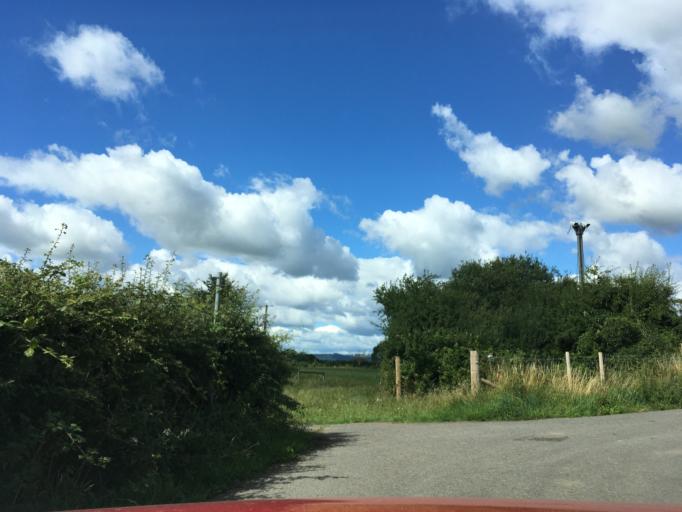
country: GB
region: England
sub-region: Gloucestershire
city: Newent
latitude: 51.8499
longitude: -2.3700
